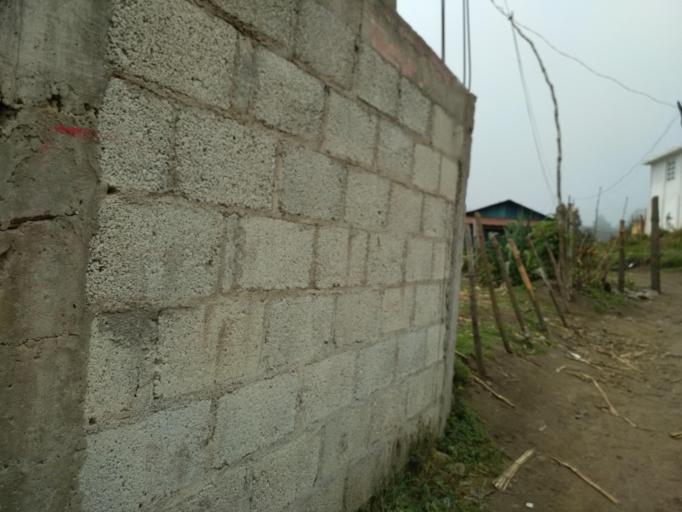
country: MX
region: Veracruz
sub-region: Mariano Escobedo
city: San Isidro el Berro
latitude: 18.9748
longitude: -97.2055
